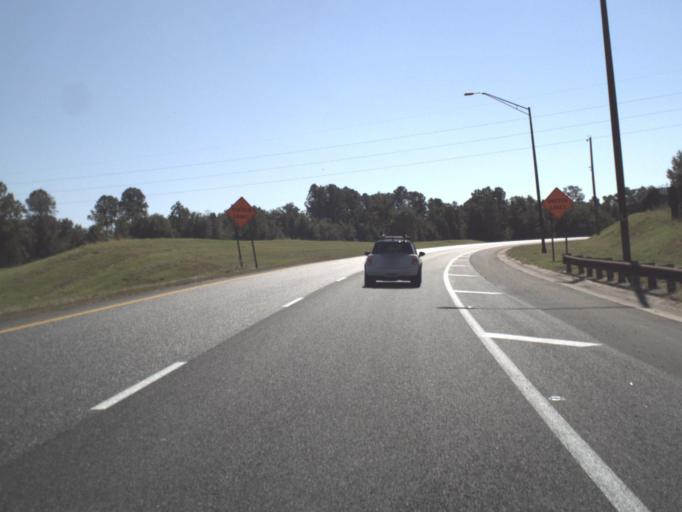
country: US
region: Florida
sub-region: Citrus County
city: Sugarmill Woods
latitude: 28.6441
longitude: -82.4903
